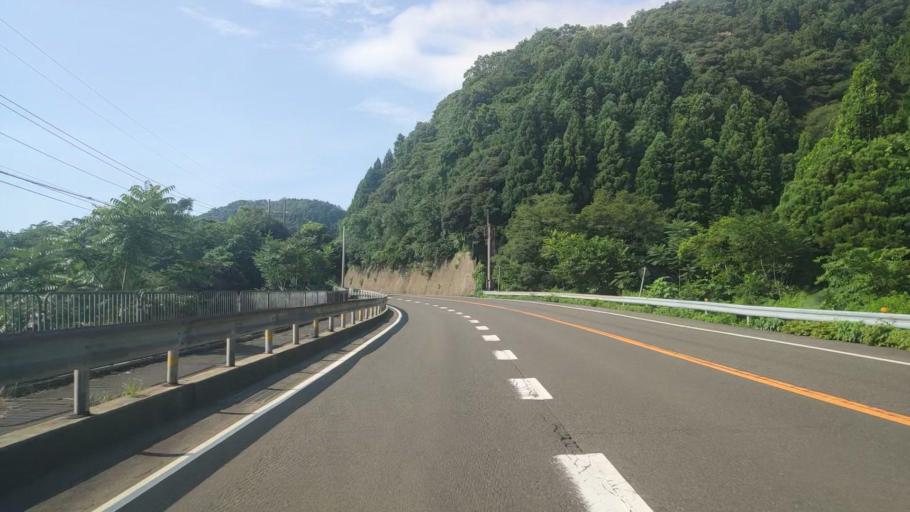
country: JP
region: Fukui
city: Tsuruga
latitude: 35.7593
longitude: 136.1050
